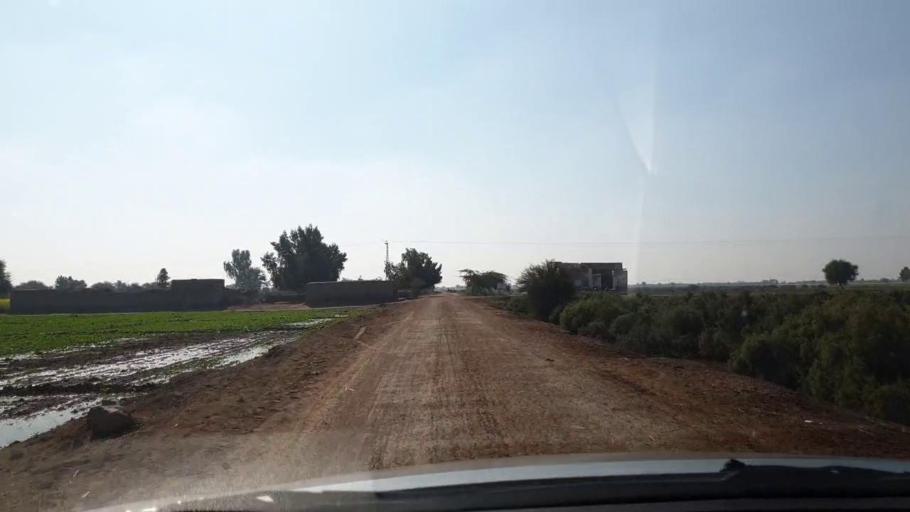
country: PK
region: Sindh
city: Jhol
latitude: 25.8773
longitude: 68.8953
